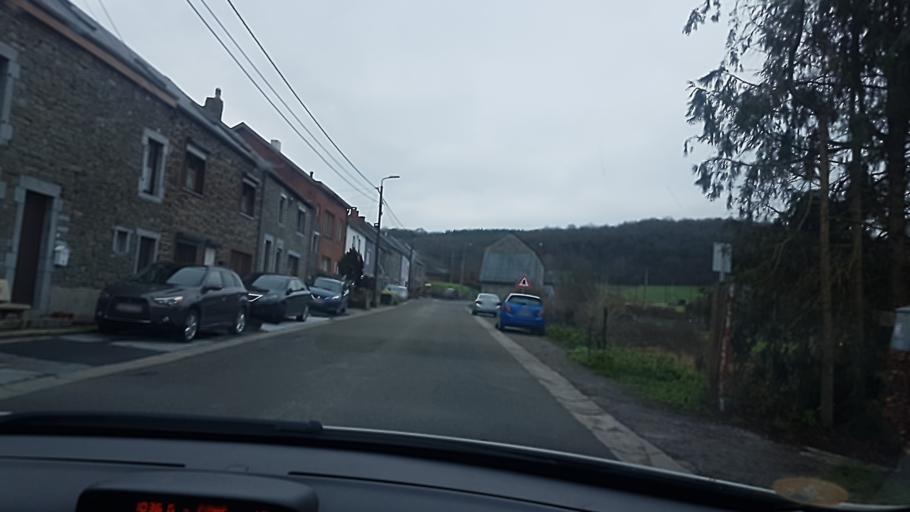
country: BE
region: Wallonia
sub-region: Province de Namur
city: Couvin
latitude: 50.0671
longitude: 4.6073
